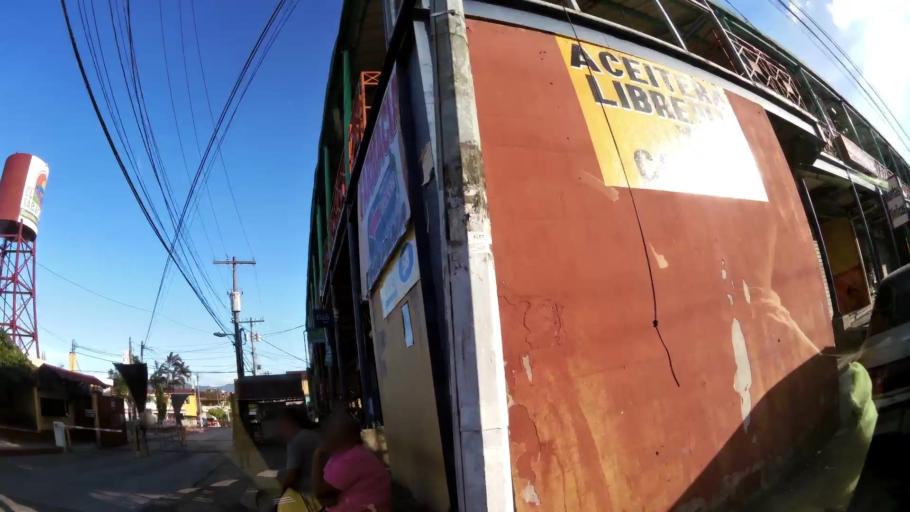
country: GT
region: Guatemala
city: Villa Nueva
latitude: 14.5198
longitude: -90.5792
